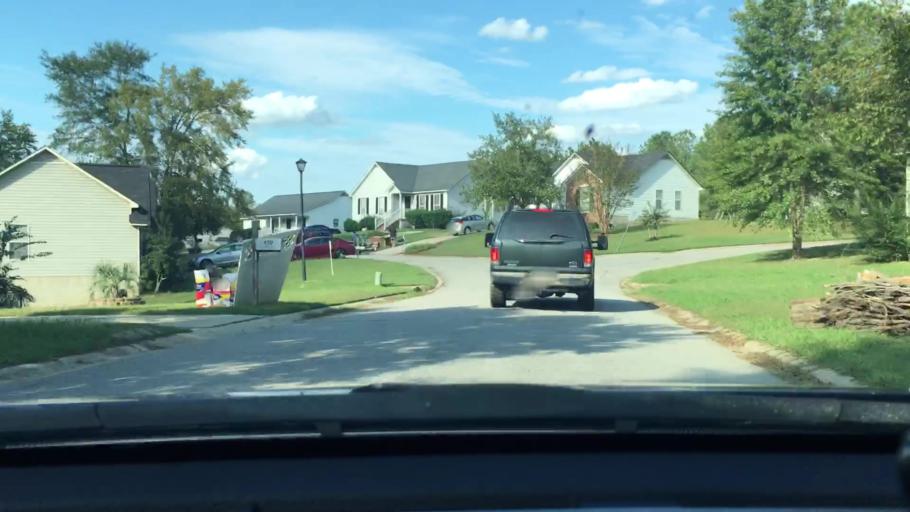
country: US
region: South Carolina
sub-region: Lexington County
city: Irmo
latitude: 34.1108
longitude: -81.1597
